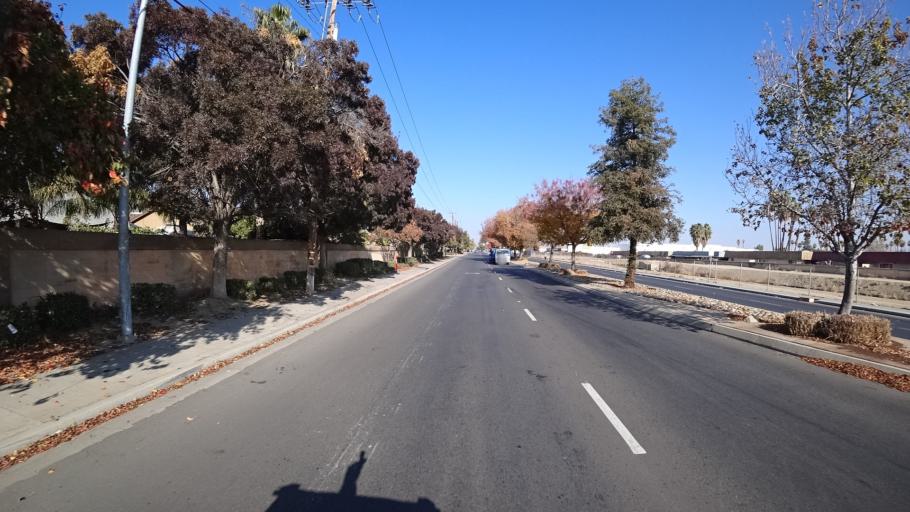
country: US
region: California
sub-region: Kern County
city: Greenfield
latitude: 35.3147
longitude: -119.0214
